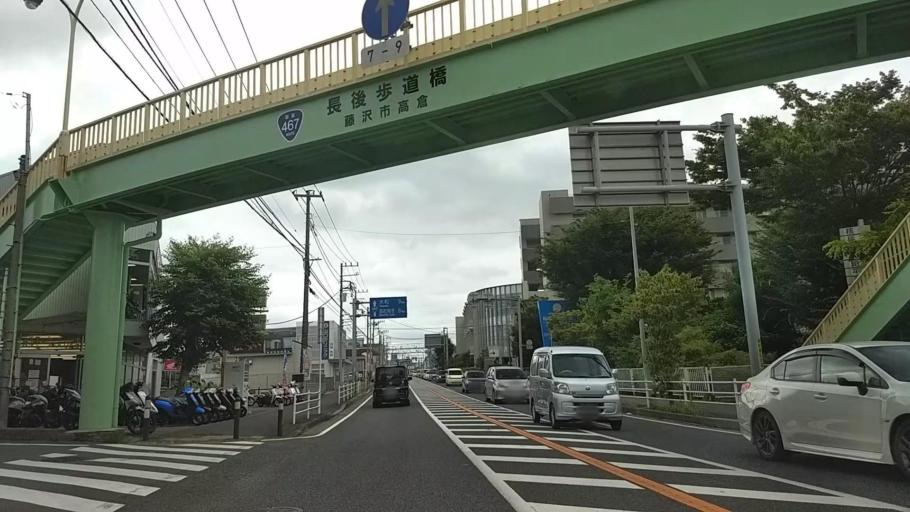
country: JP
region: Kanagawa
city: Minami-rinkan
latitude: 35.4163
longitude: 139.4697
